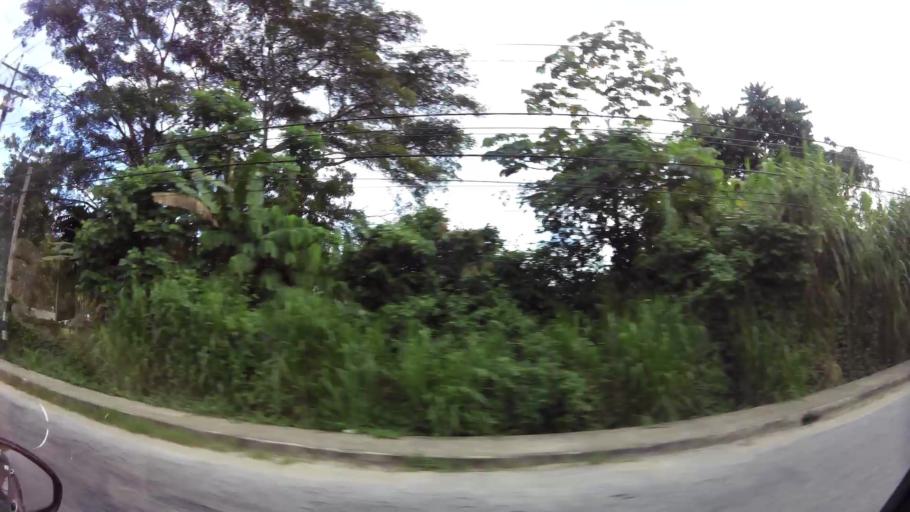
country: TT
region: Diego Martin
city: Petit Valley
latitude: 10.7104
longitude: -61.4640
